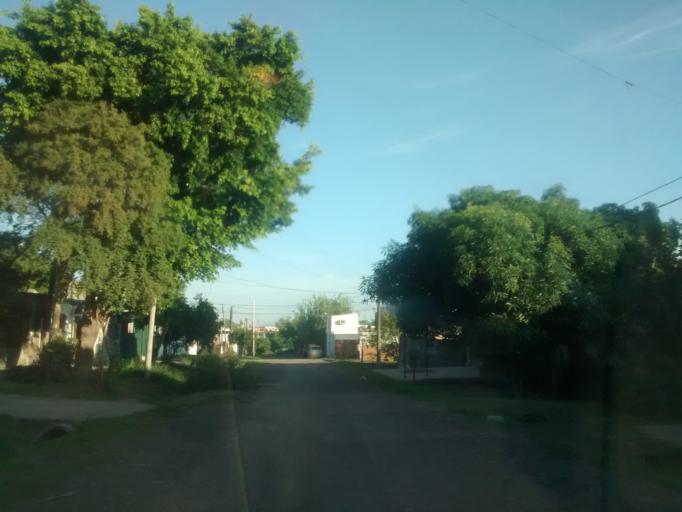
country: AR
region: Chaco
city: Resistencia
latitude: -27.4429
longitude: -58.9729
